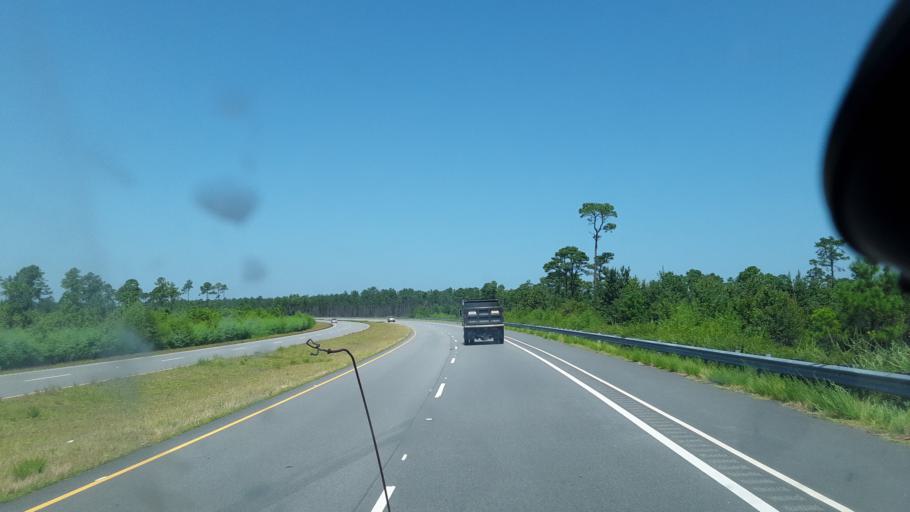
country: US
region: South Carolina
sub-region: Horry County
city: Forestbrook
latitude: 33.7999
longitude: -78.8834
